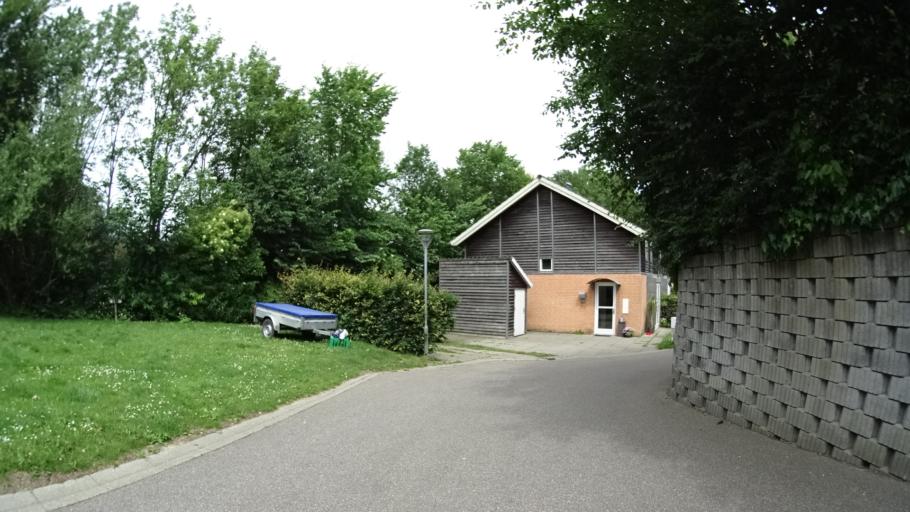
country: DK
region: Central Jutland
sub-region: Arhus Kommune
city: Stavtrup
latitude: 56.1227
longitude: 10.1312
